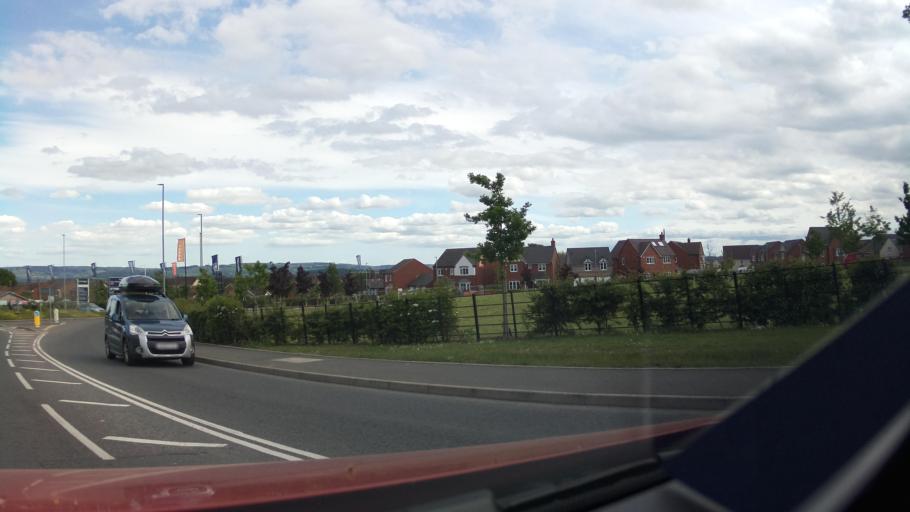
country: GB
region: England
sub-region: Worcestershire
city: Evesham
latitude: 52.0883
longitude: -1.9687
